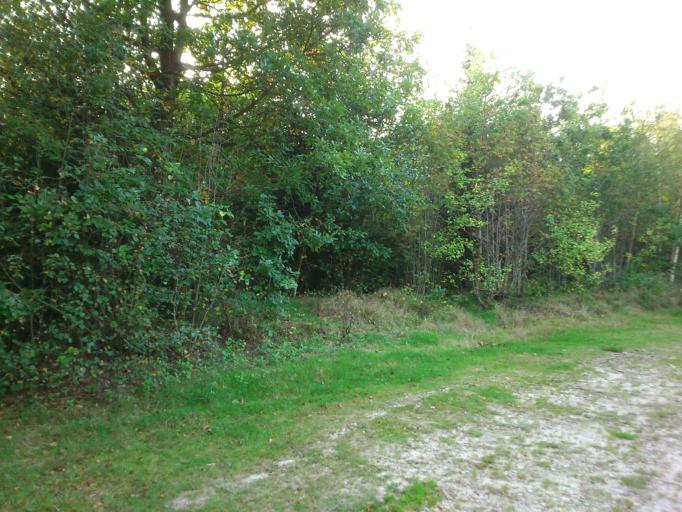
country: DK
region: Central Jutland
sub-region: Ringkobing-Skjern Kommune
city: Skjern
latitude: 56.0000
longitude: 8.4596
